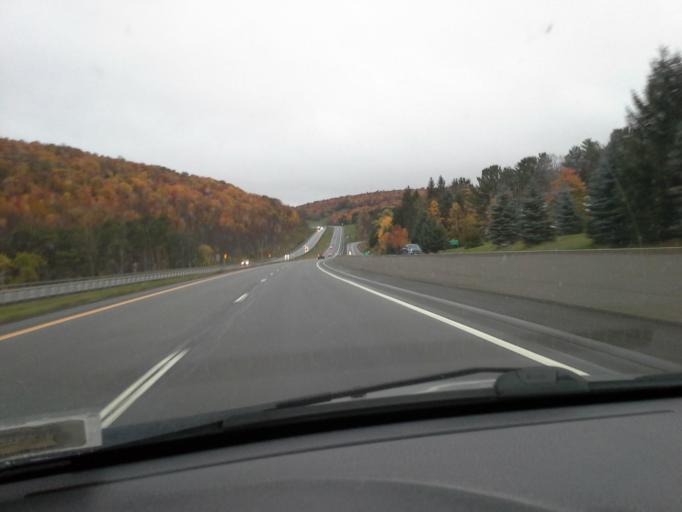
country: US
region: Pennsylvania
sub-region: Susquehanna County
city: Hallstead
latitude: 42.0887
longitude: -75.7196
